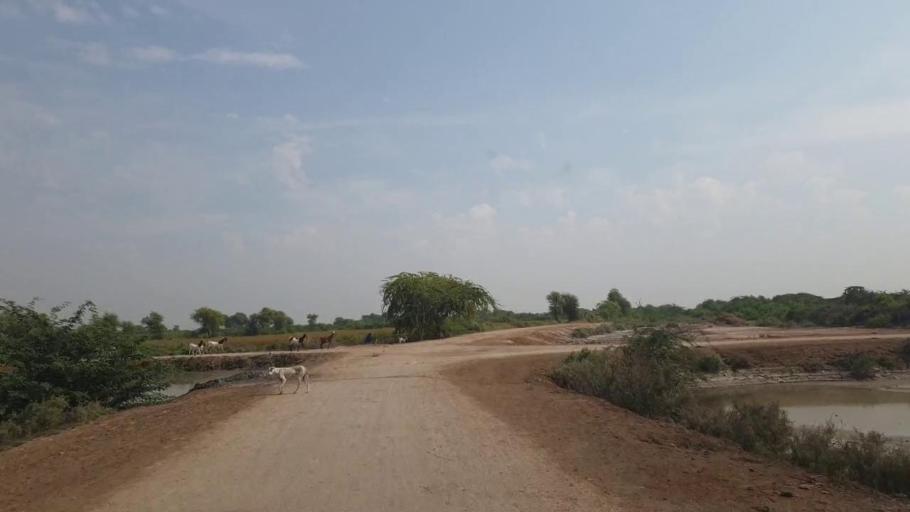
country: PK
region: Sindh
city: Rajo Khanani
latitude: 24.9562
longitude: 69.0174
